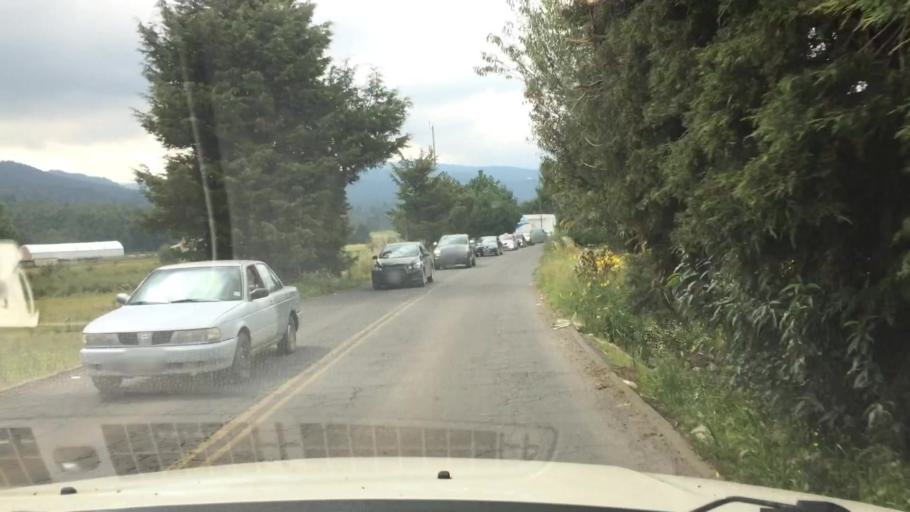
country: MX
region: Mexico City
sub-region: Tlalpan
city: Lomas de Tepemecatl
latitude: 19.2320
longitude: -99.2284
